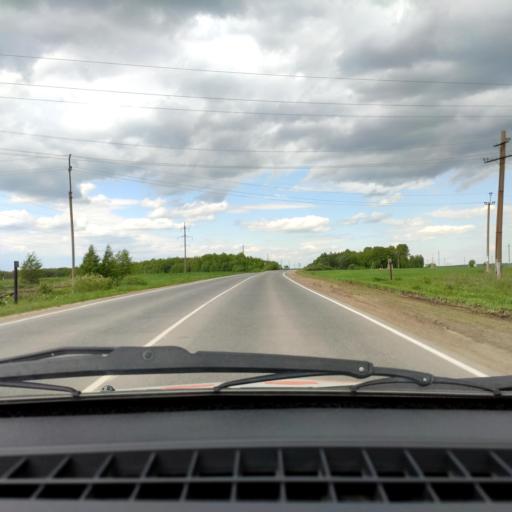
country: RU
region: Bashkortostan
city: Iglino
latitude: 54.8820
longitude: 56.4699
